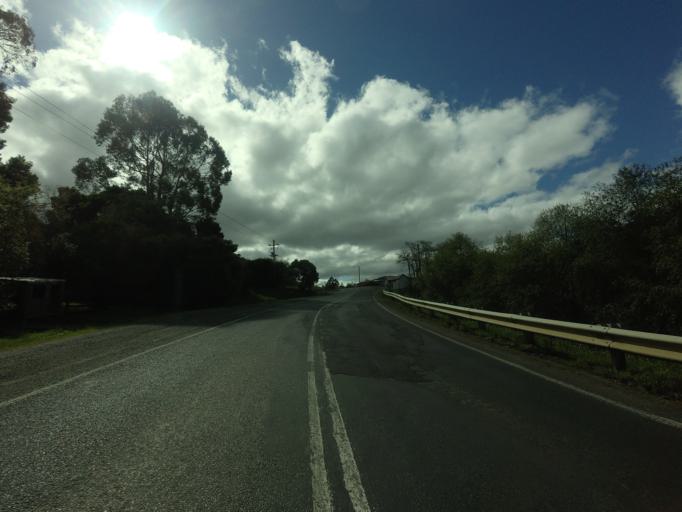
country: AU
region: Tasmania
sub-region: Huon Valley
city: Geeveston
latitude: -43.3032
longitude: 147.0072
